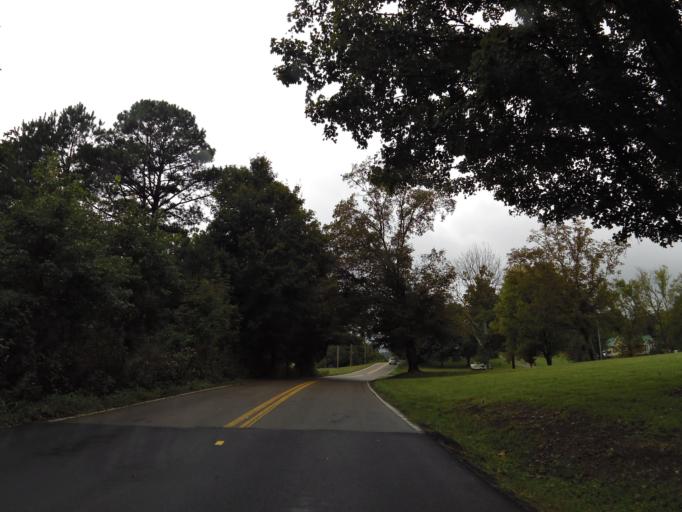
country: US
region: Tennessee
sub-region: Bradley County
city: Cleveland
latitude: 35.1789
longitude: -84.9262
